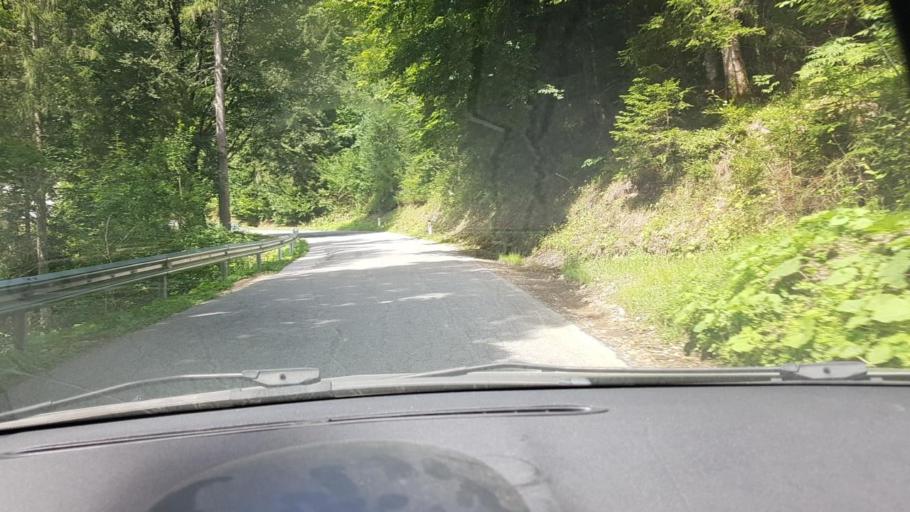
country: SI
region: Solcava
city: Solcava
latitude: 46.4198
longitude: 14.6233
